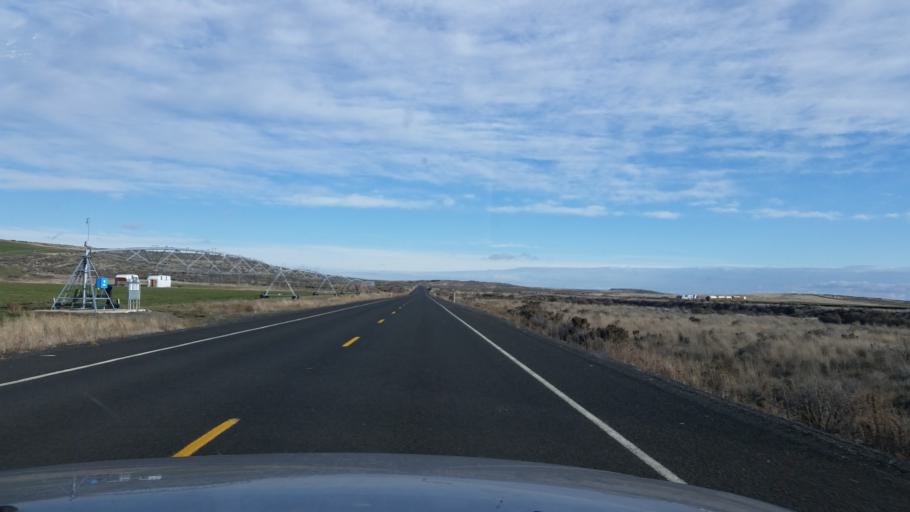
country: US
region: Washington
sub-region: Adams County
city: Ritzville
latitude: 47.3385
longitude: -118.6333
